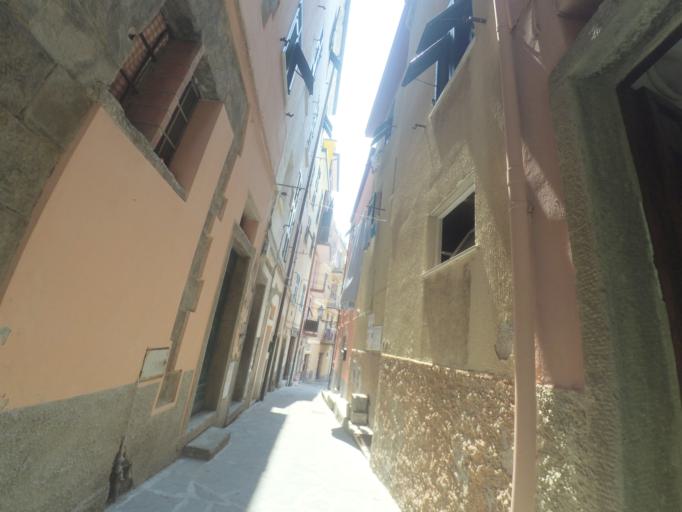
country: IT
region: Liguria
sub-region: Provincia di La Spezia
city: Riomaggiore
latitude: 44.1071
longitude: 9.7299
